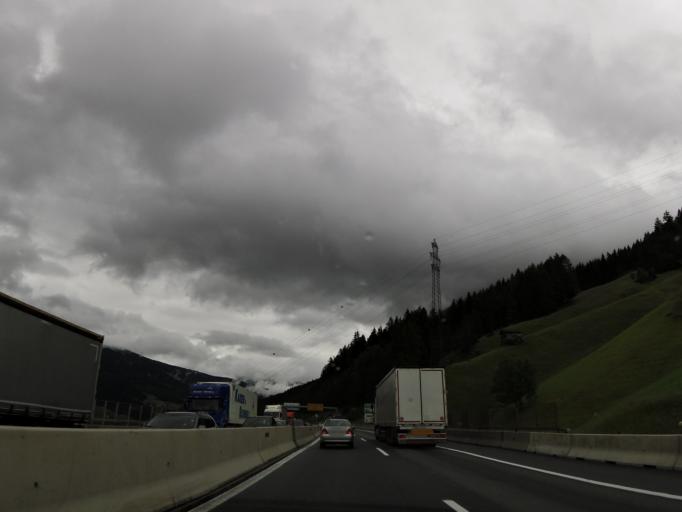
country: AT
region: Tyrol
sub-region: Politischer Bezirk Innsbruck Land
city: Schoenberg im Stubaital
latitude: 47.1818
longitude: 11.4105
